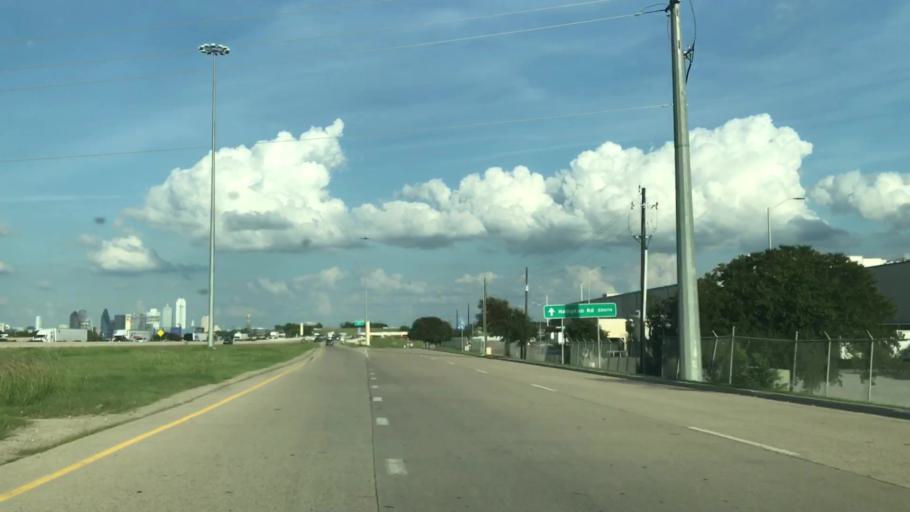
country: US
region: Texas
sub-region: Dallas County
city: Cockrell Hill
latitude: 32.7667
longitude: -96.8674
